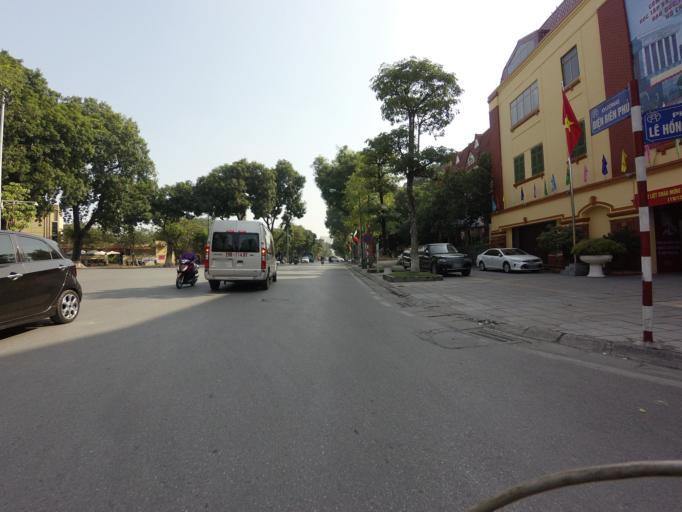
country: VN
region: Ha Noi
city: Hanoi
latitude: 21.0333
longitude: 105.8385
